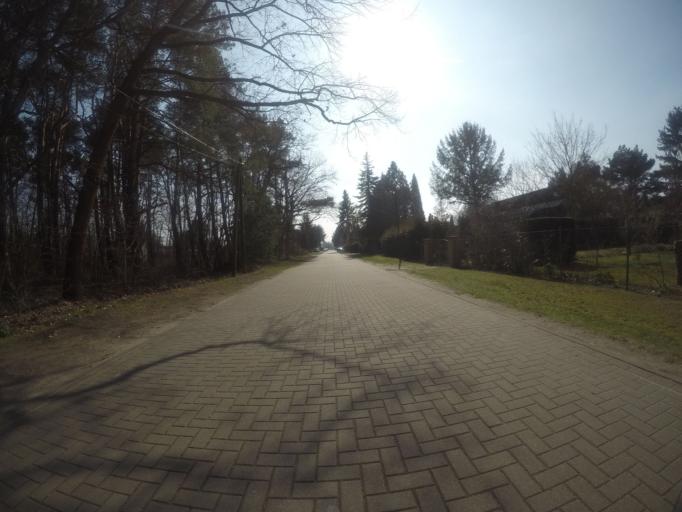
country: DE
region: Brandenburg
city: Bestensee
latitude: 52.2878
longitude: 13.7480
